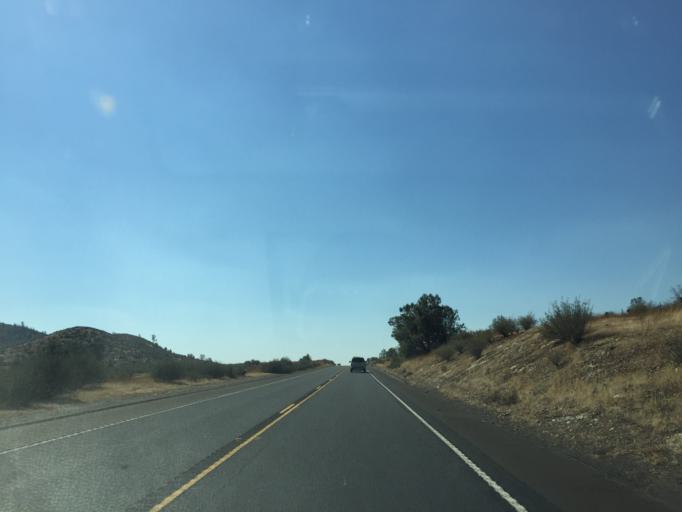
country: US
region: California
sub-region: Tuolumne County
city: Jamestown
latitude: 37.8725
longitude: -120.5092
